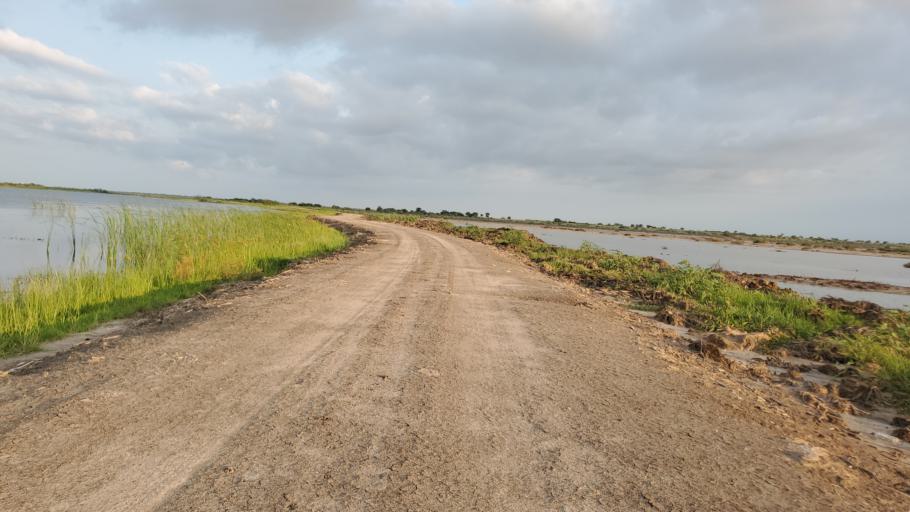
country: SN
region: Saint-Louis
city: Saint-Louis
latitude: 16.0211
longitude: -16.4077
